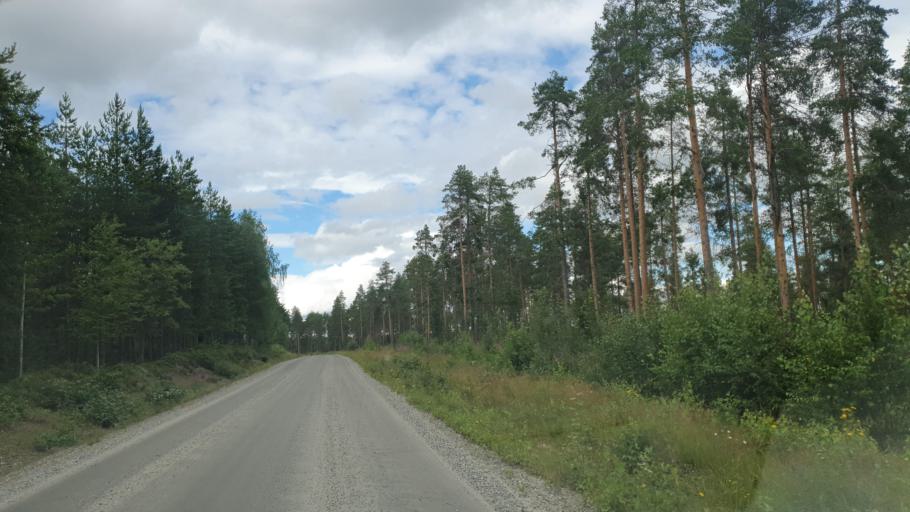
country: FI
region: Kainuu
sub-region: Kehys-Kainuu
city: Kuhmo
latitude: 64.0960
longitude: 29.4144
